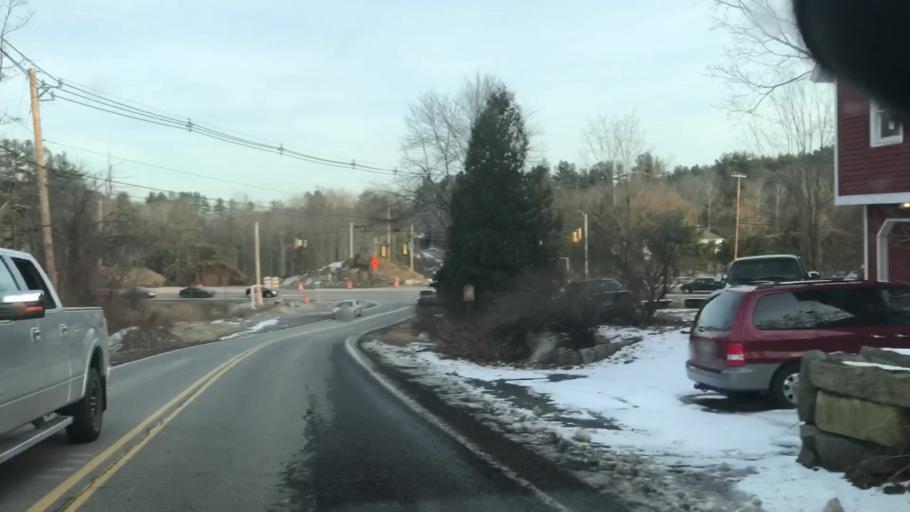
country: US
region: New Hampshire
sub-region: Hillsborough County
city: Bedford
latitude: 42.9465
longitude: -71.5146
